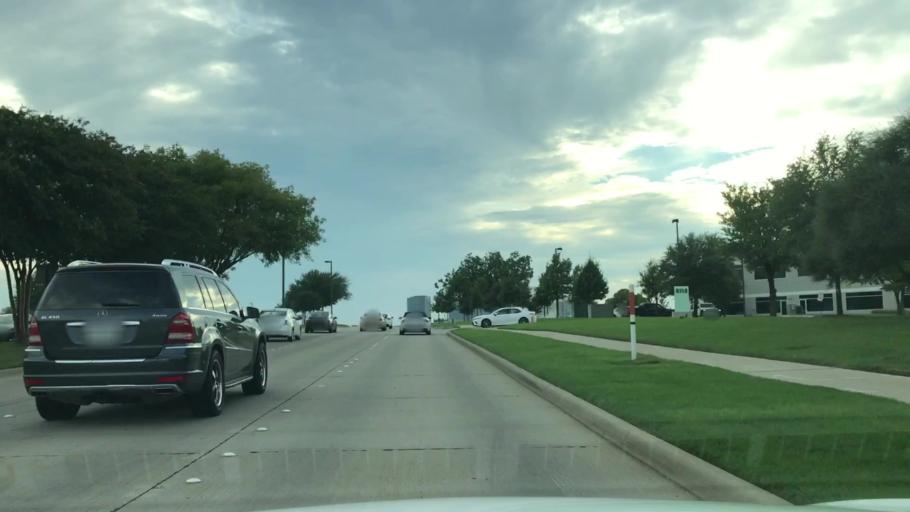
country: US
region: Texas
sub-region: Collin County
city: Frisco
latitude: 33.0882
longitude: -96.8062
